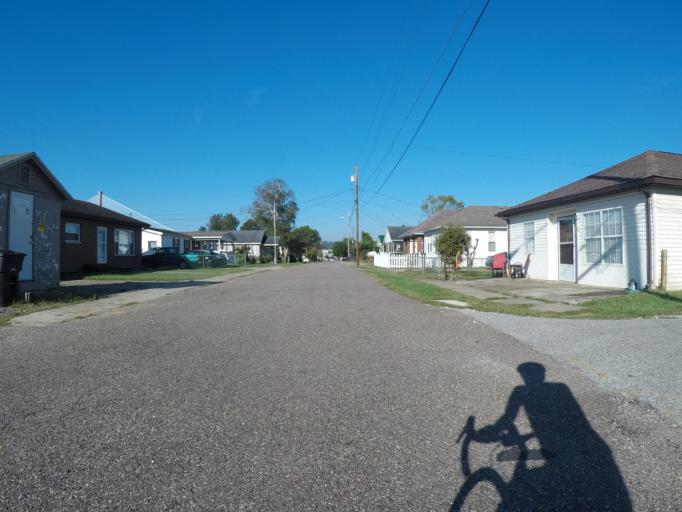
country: US
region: West Virginia
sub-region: Cabell County
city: Huntington
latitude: 38.4376
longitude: -82.3828
